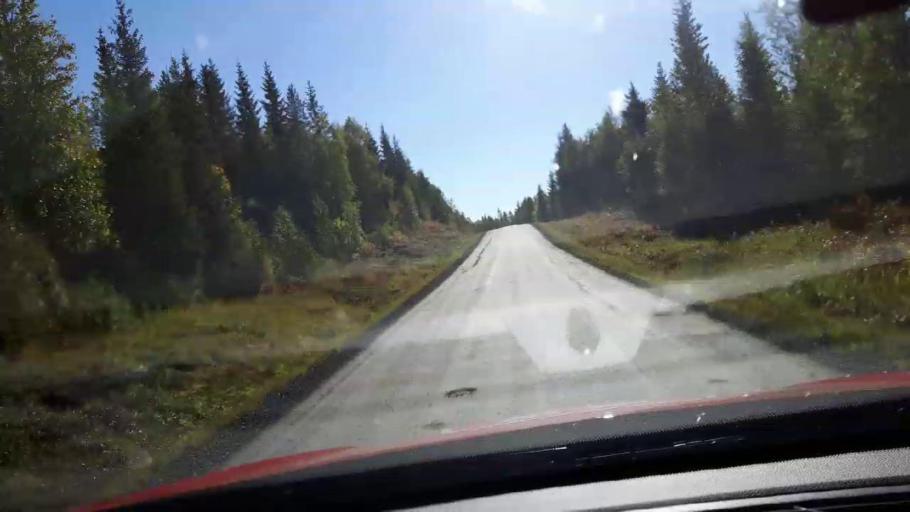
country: NO
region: Nord-Trondelag
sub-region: Lierne
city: Sandvika
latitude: 64.6002
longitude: 13.9723
